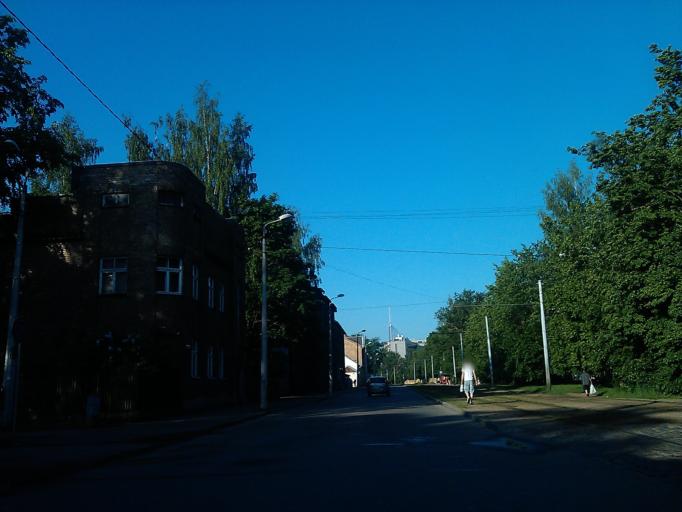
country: LV
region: Riga
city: Jaunciems
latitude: 56.9784
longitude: 24.1742
